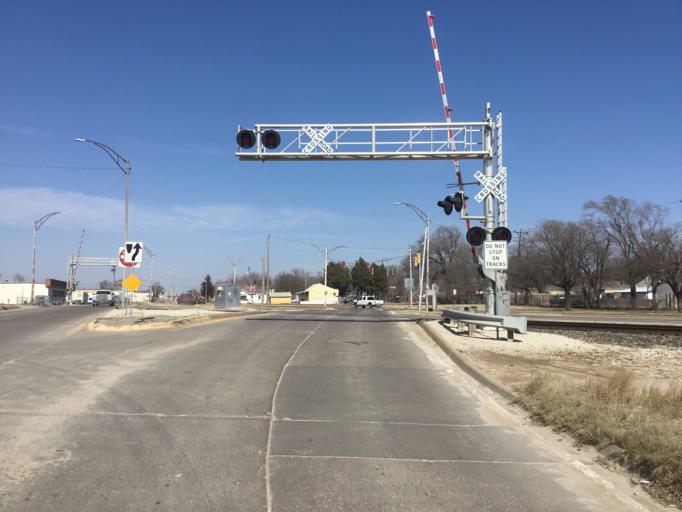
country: US
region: Kansas
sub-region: Sedgwick County
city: Wichita
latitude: 37.6679
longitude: -97.3263
